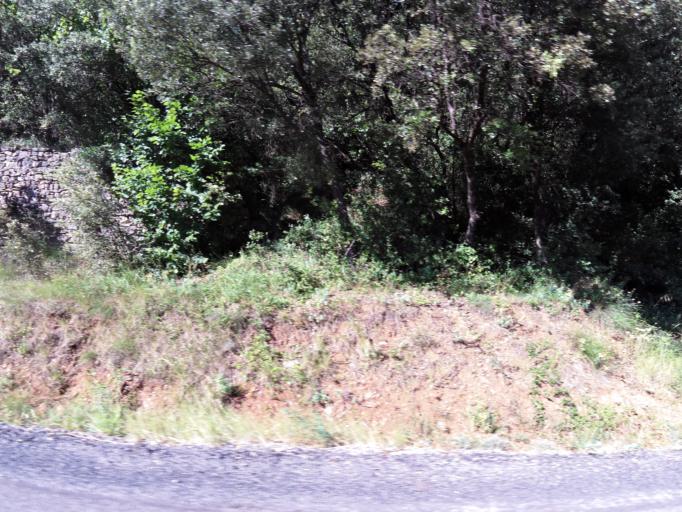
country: FR
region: Languedoc-Roussillon
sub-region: Departement du Gard
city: Saint-Jean-du-Gard
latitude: 44.0793
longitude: 3.9270
